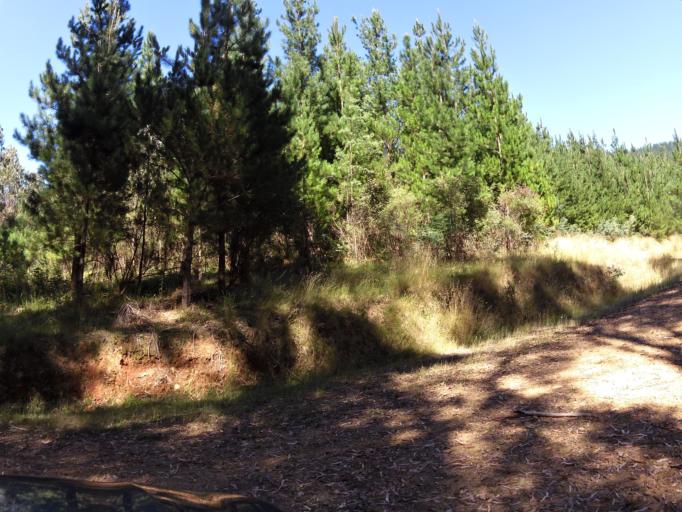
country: AU
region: Victoria
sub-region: Alpine
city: Mount Beauty
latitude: -36.7522
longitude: 146.9556
